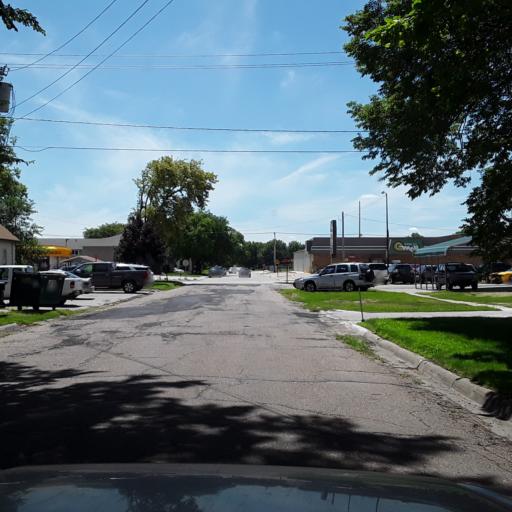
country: US
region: Nebraska
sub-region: Merrick County
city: Central City
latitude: 41.1169
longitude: -97.9976
